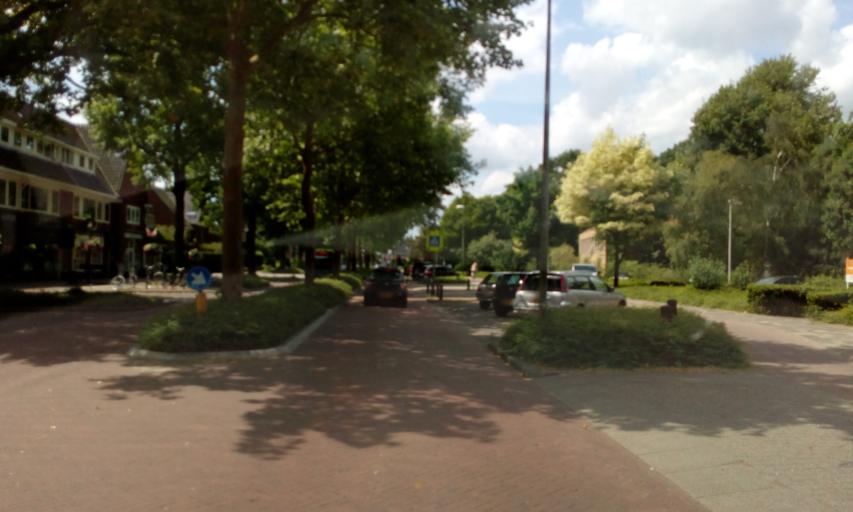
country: NL
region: North Holland
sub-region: Gemeente Bussum
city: Bussum
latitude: 52.2765
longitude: 5.1773
